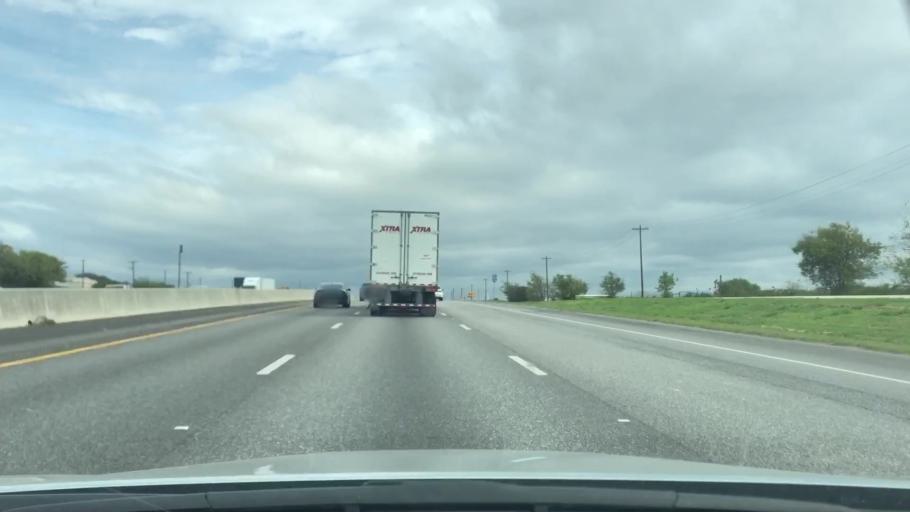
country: US
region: Texas
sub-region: Guadalupe County
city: Redwood
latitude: 29.7988
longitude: -98.0176
